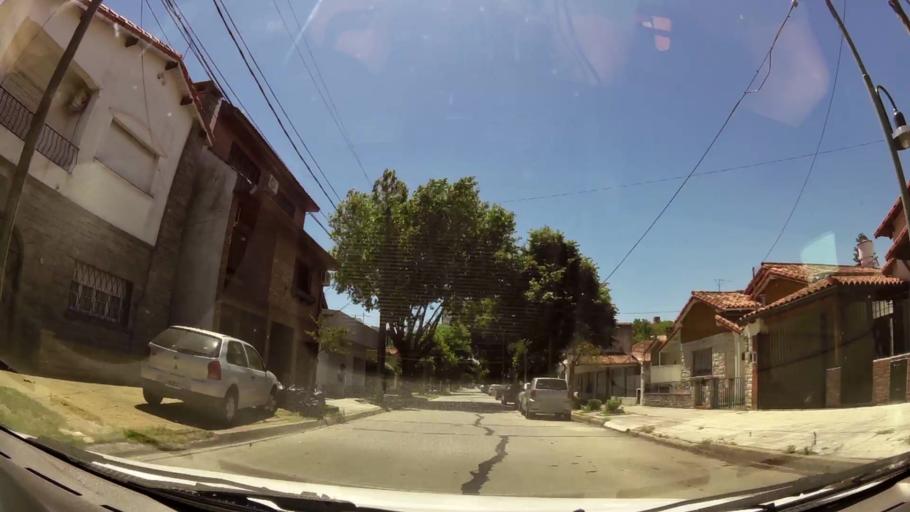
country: AR
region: Buenos Aires
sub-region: Partido de Vicente Lopez
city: Olivos
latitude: -34.5023
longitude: -58.4991
